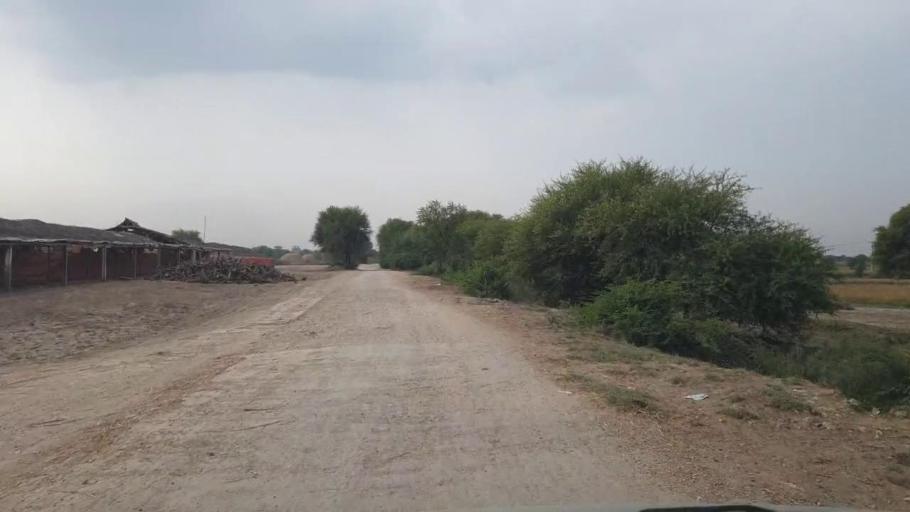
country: PK
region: Sindh
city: Talhar
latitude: 24.9176
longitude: 68.7769
